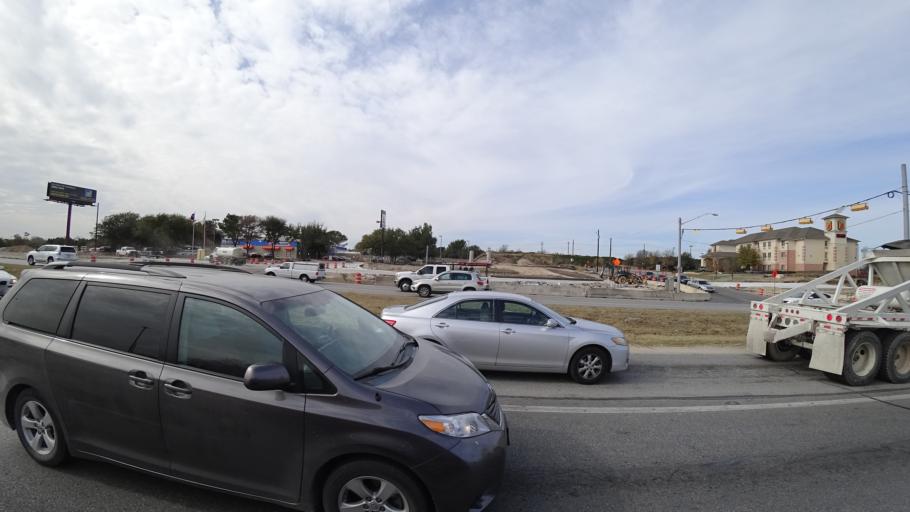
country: US
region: Texas
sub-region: Travis County
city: Austin
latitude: 30.2919
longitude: -97.6636
